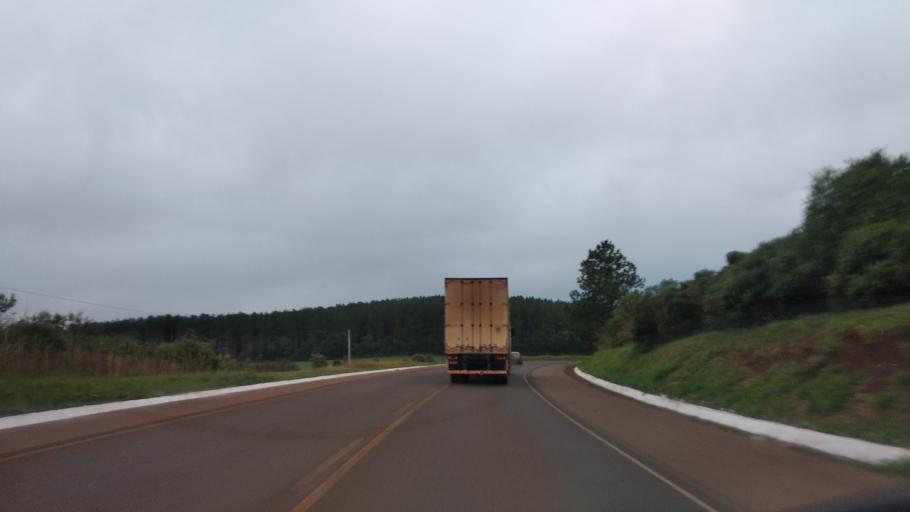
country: BR
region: Santa Catarina
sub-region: Campos Novos
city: Campos Novos
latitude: -27.3976
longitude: -51.0418
